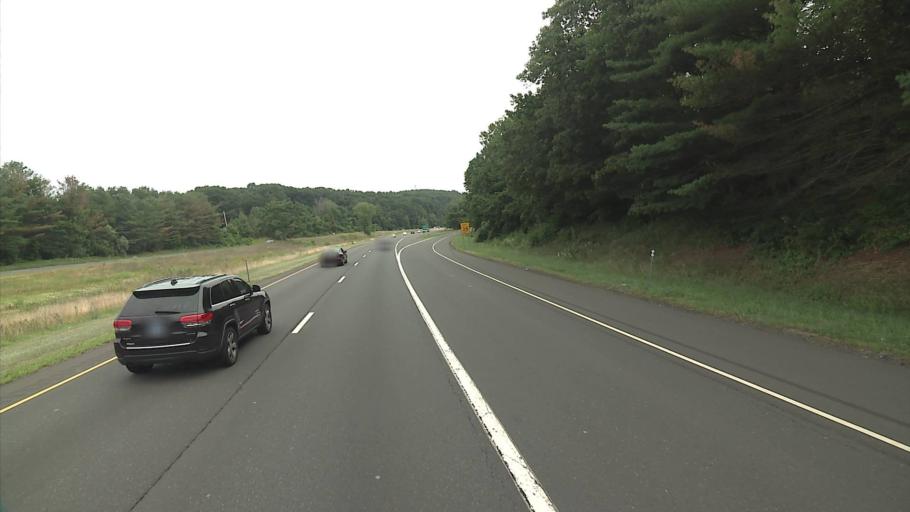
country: US
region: Connecticut
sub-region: New Haven County
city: Heritage Village
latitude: 41.4432
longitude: -73.2493
